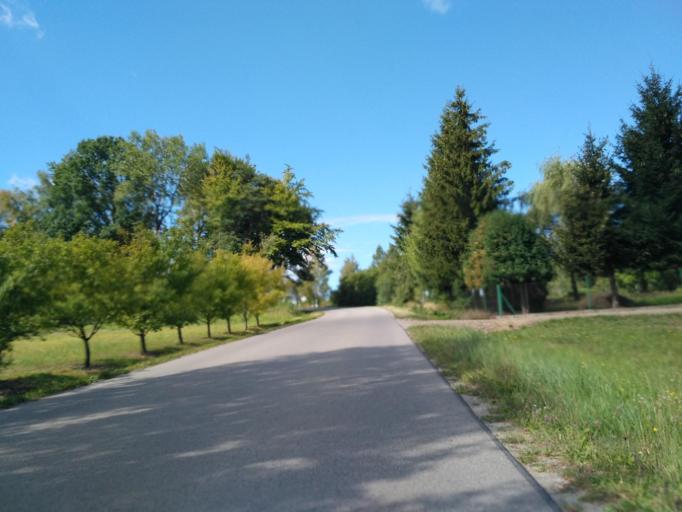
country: PL
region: Subcarpathian Voivodeship
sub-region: Powiat jasielski
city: Brzyska
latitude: 49.7809
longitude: 21.3710
